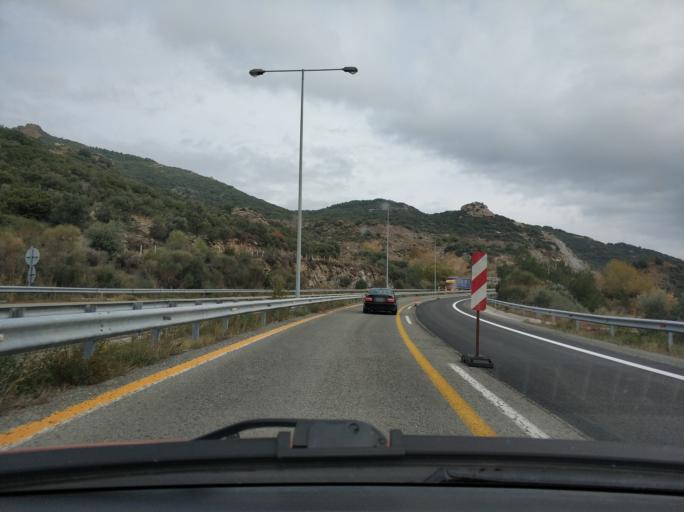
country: GR
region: East Macedonia and Thrace
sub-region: Nomos Kavalas
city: Palaio Tsifliki
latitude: 40.9090
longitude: 24.3441
